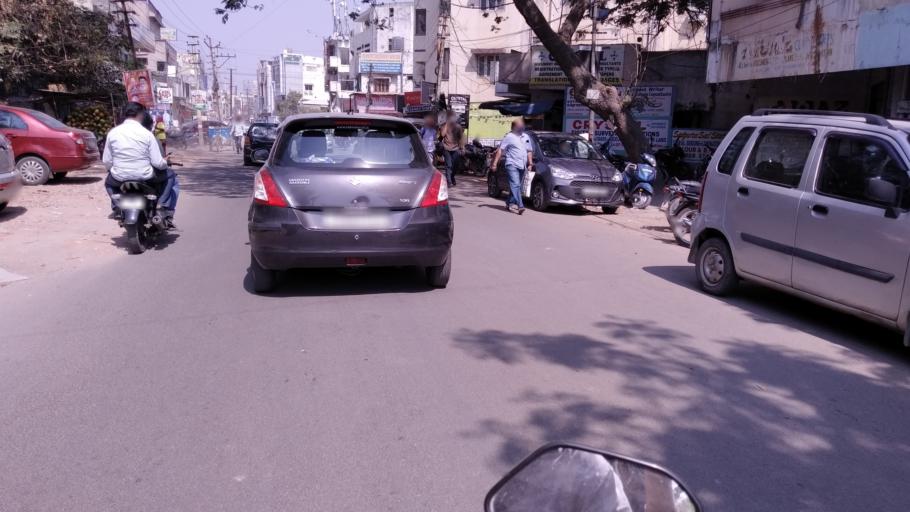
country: IN
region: Telangana
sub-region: Rangareddi
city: Quthbullapur
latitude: 17.4636
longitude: 78.4838
